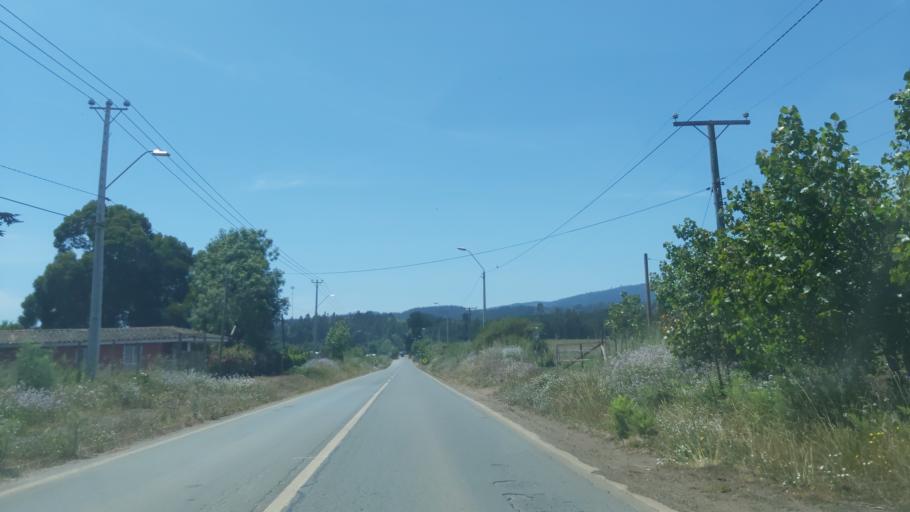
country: CL
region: Maule
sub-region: Provincia de Cauquenes
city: Cauquenes
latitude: -35.7952
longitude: -72.5486
